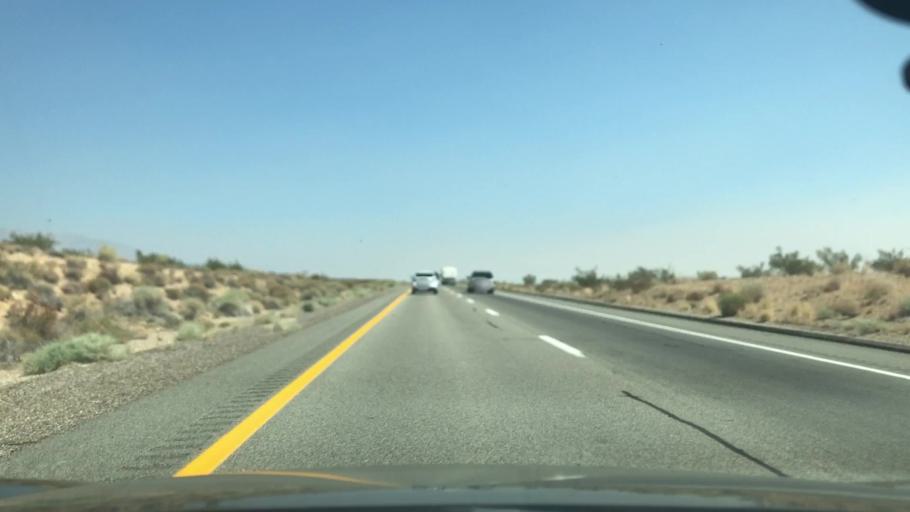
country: US
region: California
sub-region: Inyo County
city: Lone Pine
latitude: 36.1296
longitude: -117.9727
